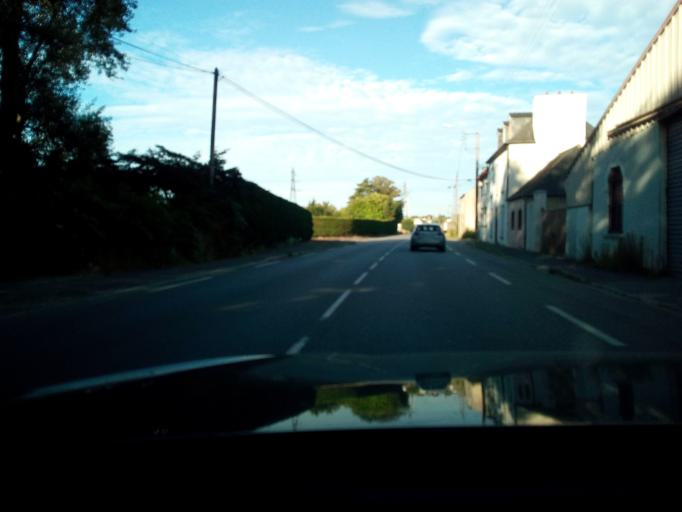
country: FR
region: Brittany
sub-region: Departement du Finistere
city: Landerneau
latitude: 48.4611
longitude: -4.2342
